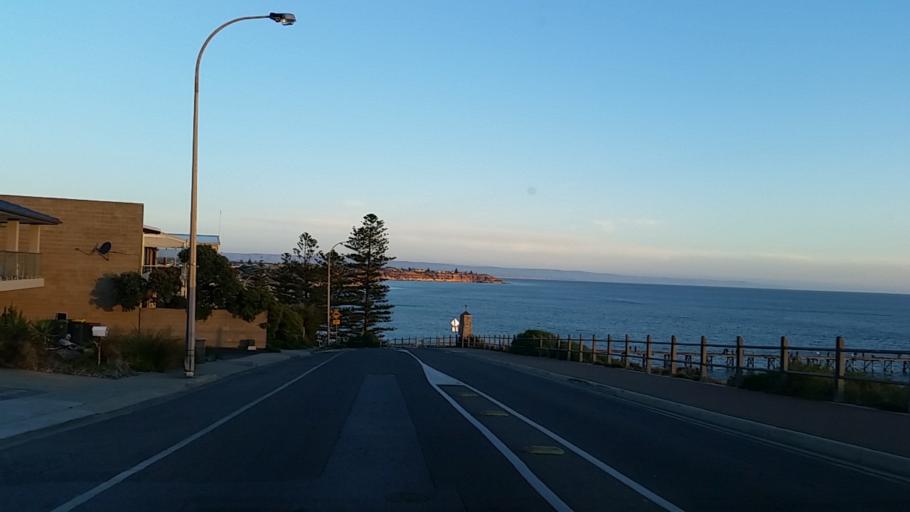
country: AU
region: South Australia
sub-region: Adelaide
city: Port Noarlunga
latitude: -35.1471
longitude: 138.4673
